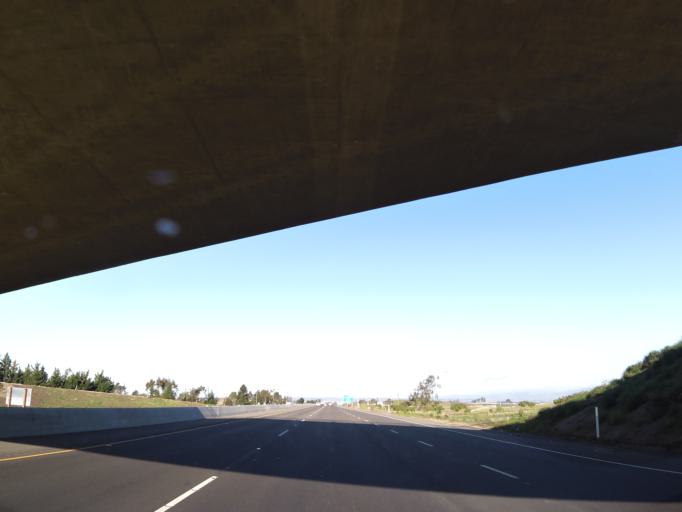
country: US
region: California
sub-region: Santa Barbara County
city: Orcutt
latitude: 34.8799
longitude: -120.4085
